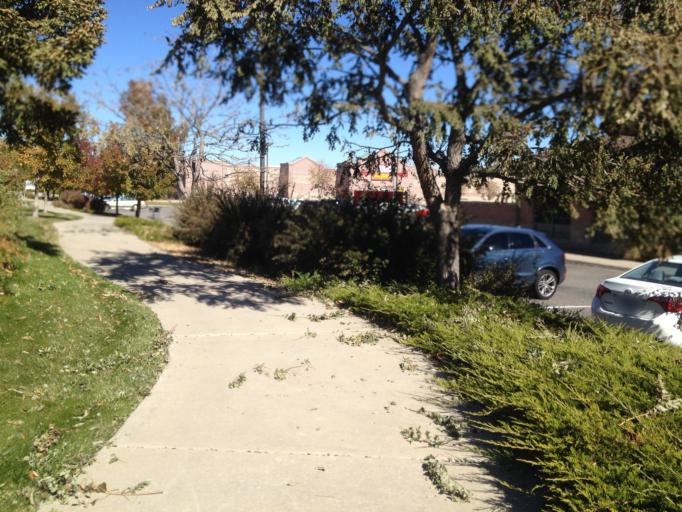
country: US
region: Colorado
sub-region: Boulder County
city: Lafayette
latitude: 40.0005
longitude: -105.1026
